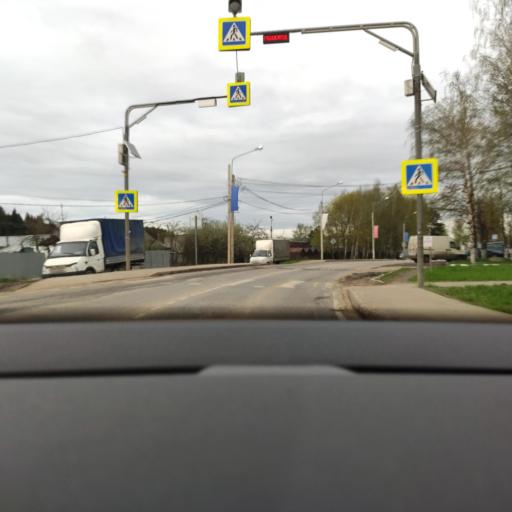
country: RU
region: Moskovskaya
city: Novopodrezkovo
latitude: 55.9955
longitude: 37.3401
